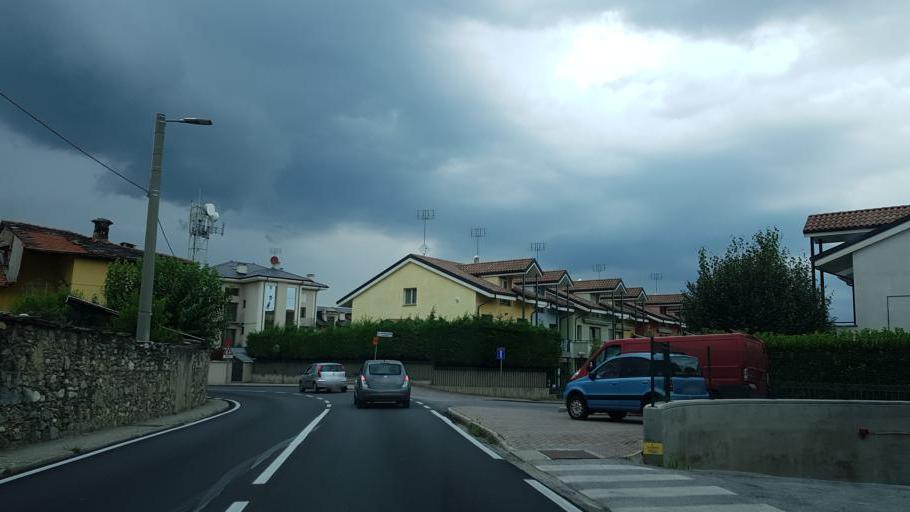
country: IT
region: Piedmont
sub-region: Provincia di Cuneo
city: Caraglio
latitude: 44.4205
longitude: 7.4325
